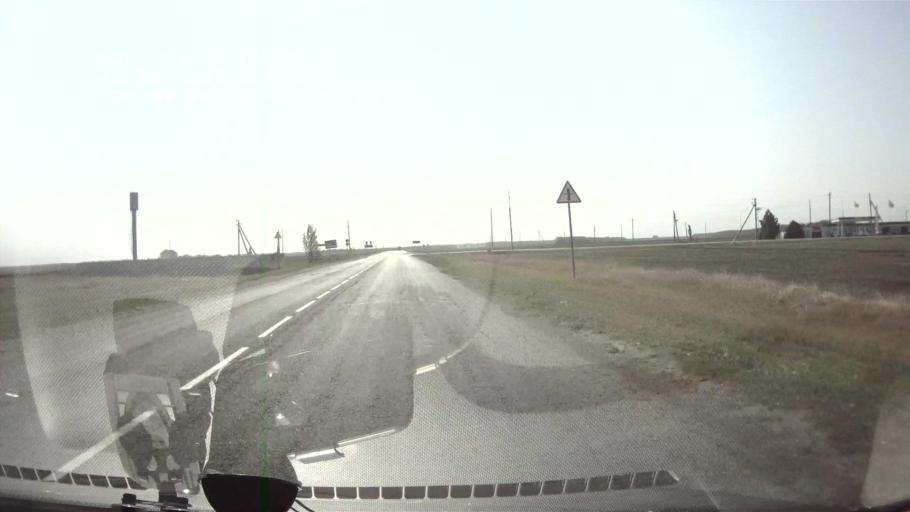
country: RU
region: Krasnodarskiy
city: Novopokrovskaya
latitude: 45.9266
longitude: 40.7118
